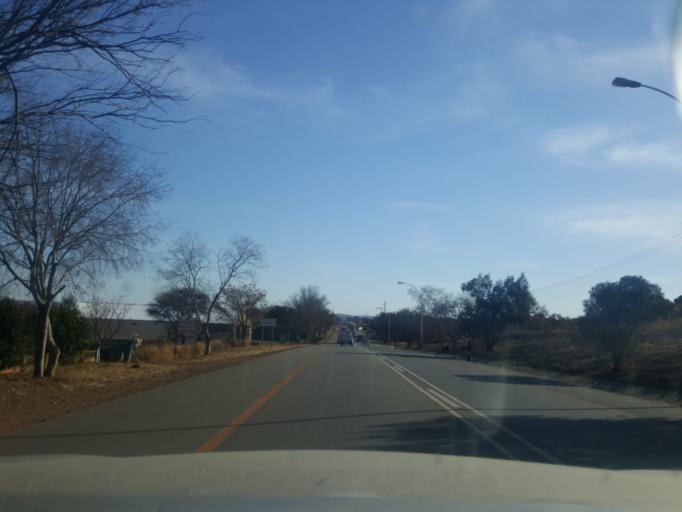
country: ZA
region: North-West
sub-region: Ngaka Modiri Molema District Municipality
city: Zeerust
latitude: -25.5422
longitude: 26.0919
